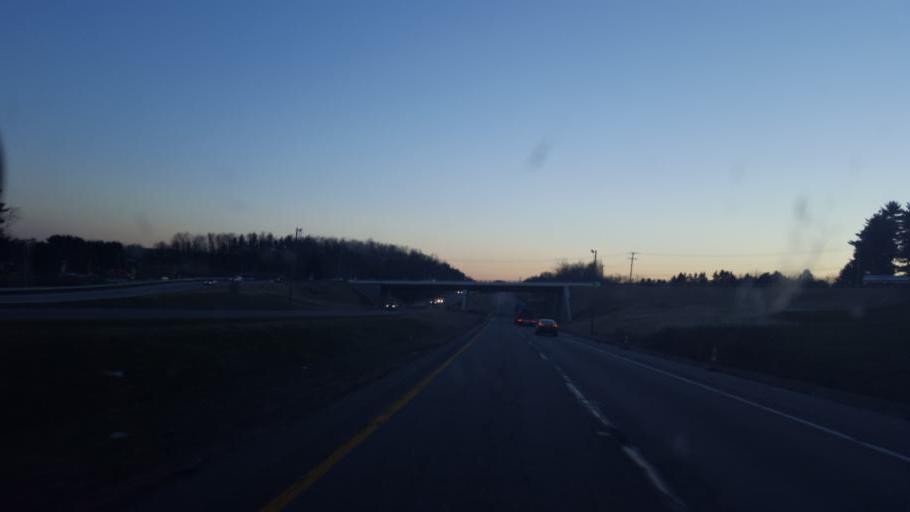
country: US
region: Ohio
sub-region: Belmont County
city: Saint Clairsville
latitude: 40.0753
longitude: -80.9653
